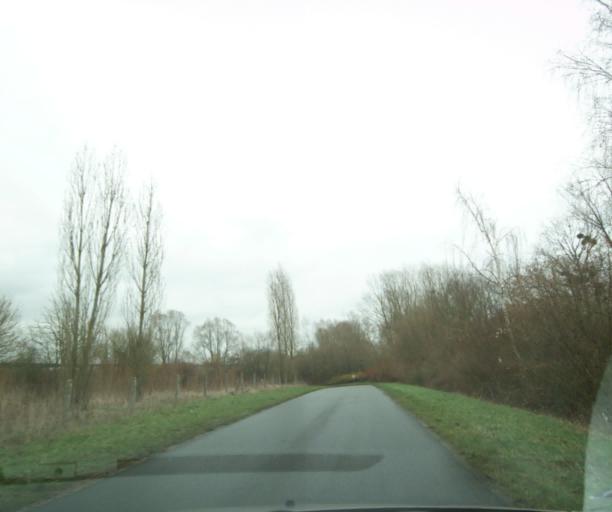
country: FR
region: Picardie
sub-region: Departement de l'Oise
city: Noyon
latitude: 49.5679
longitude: 2.9950
